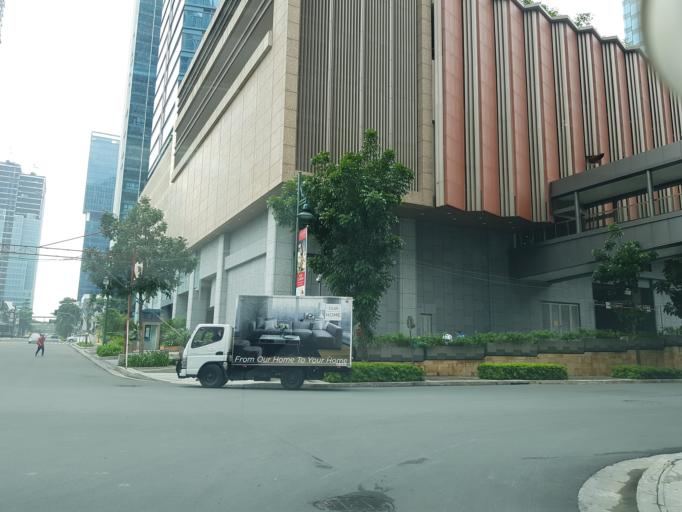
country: PH
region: Metro Manila
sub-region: Makati City
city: Makati City
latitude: 14.5582
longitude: 121.0517
